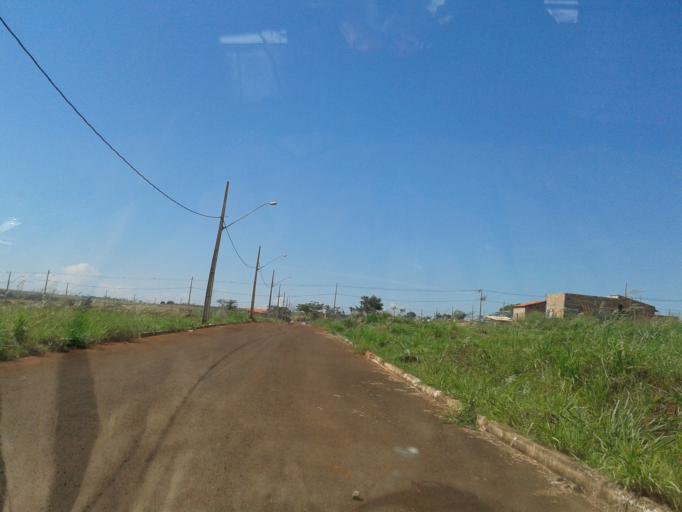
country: BR
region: Goias
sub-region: Itumbiara
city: Itumbiara
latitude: -18.4240
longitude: -49.1851
